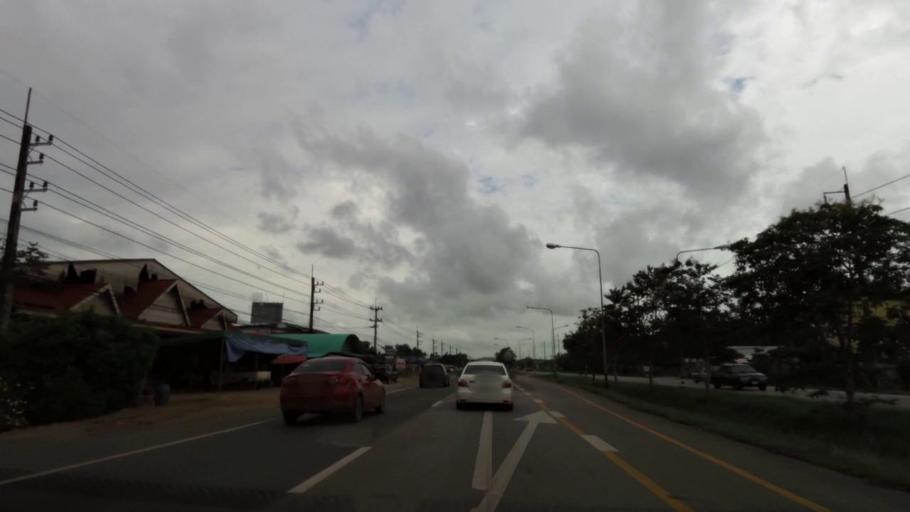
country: TH
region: Chanthaburi
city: Na Yai Am
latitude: 12.7256
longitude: 101.9329
